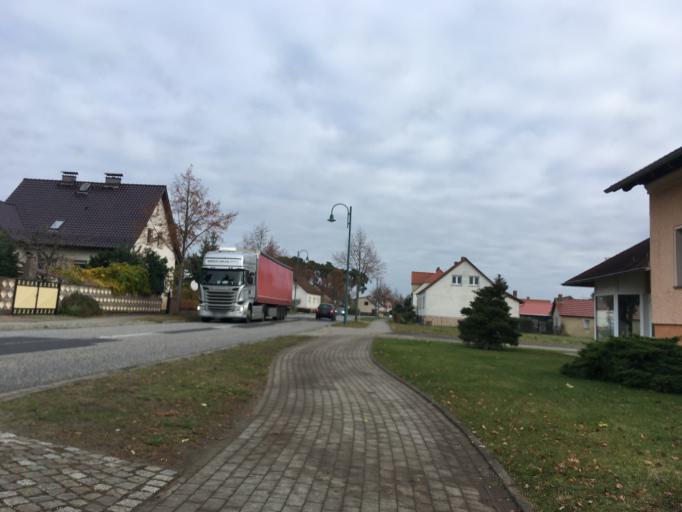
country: DE
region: Brandenburg
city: Tauer
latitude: 51.8913
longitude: 14.4384
